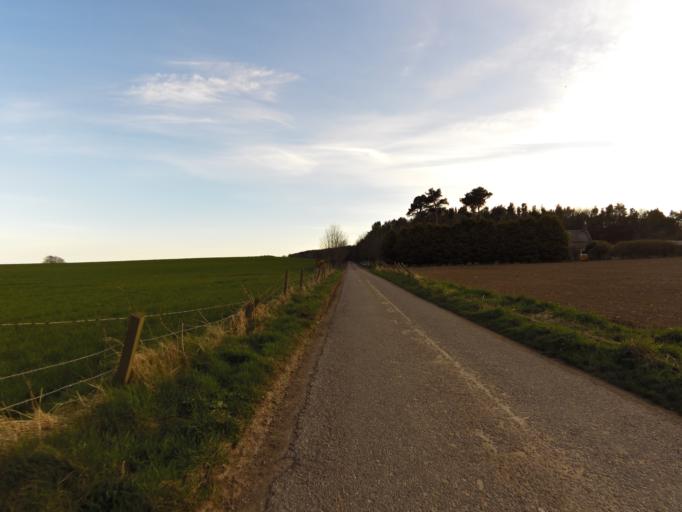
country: GB
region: Scotland
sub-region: Aberdeenshire
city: Stonehaven
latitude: 56.9293
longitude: -2.2278
